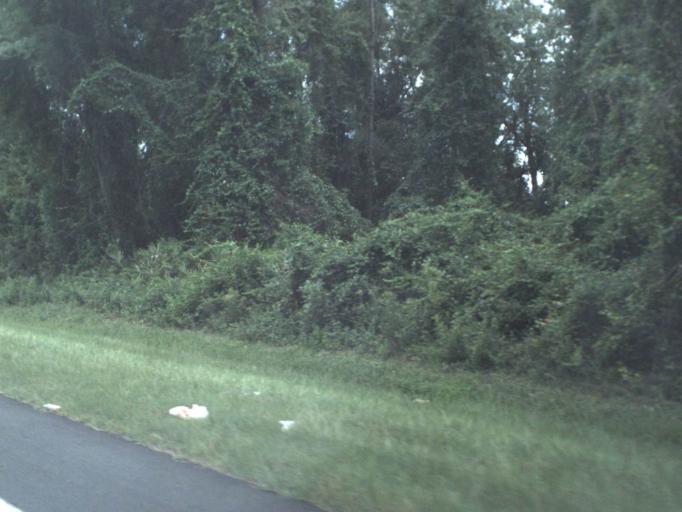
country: US
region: Florida
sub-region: Union County
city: Lake Butler
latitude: 30.0789
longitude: -82.4499
